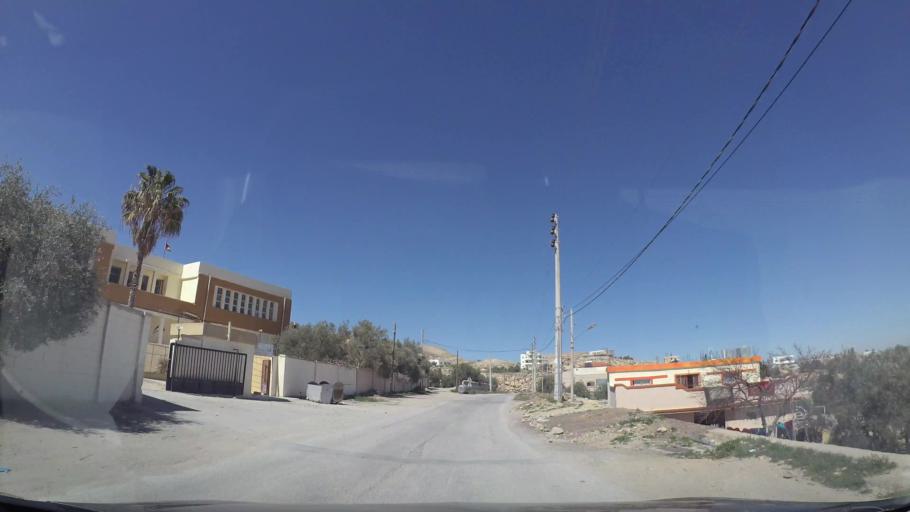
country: JO
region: Tafielah
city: At Tafilah
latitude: 30.8233
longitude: 35.5809
